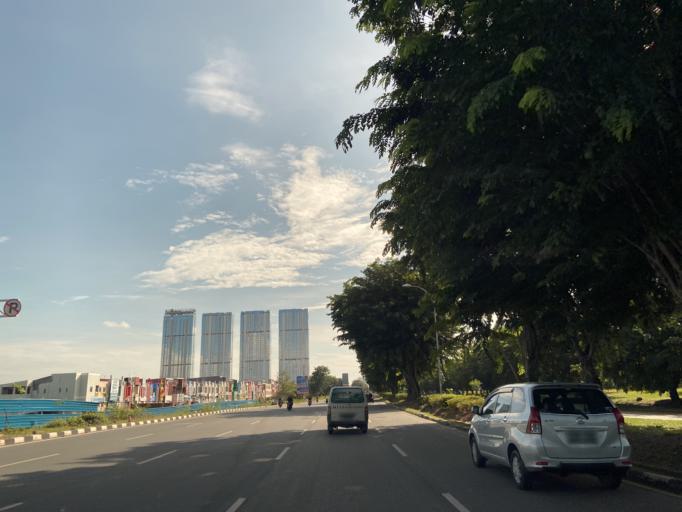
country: SG
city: Singapore
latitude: 1.1128
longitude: 104.0427
